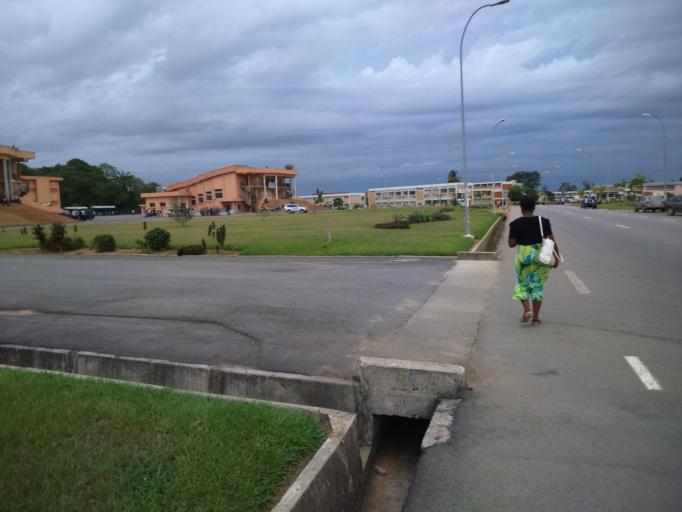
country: CI
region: Lagunes
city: Abidjan
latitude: 5.3477
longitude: -3.9878
